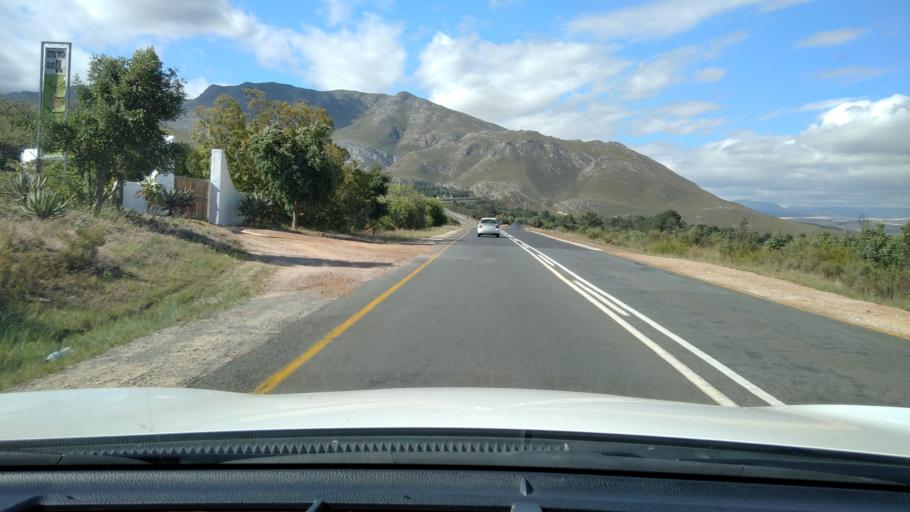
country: ZA
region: Western Cape
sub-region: Overberg District Municipality
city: Grabouw
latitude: -34.2337
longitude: 19.1864
